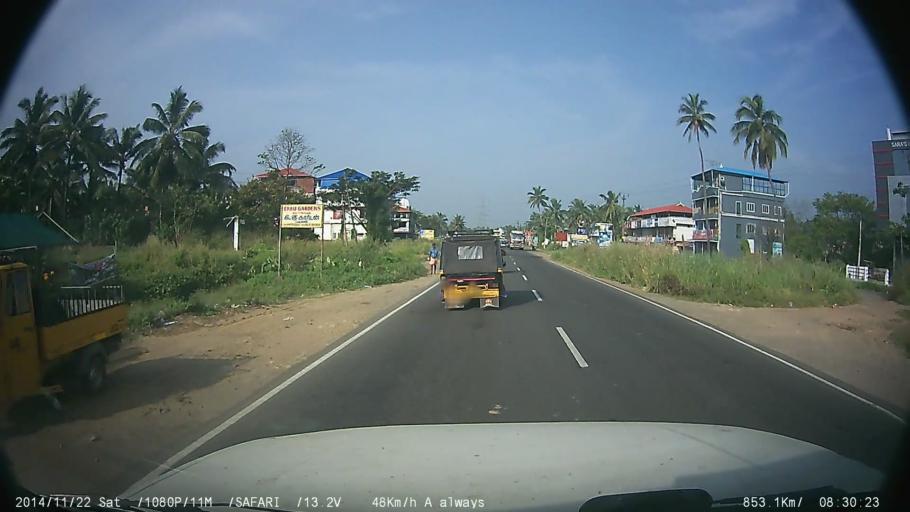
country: IN
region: Kerala
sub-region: Thrissur District
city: Trichur
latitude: 10.5563
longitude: 76.3252
